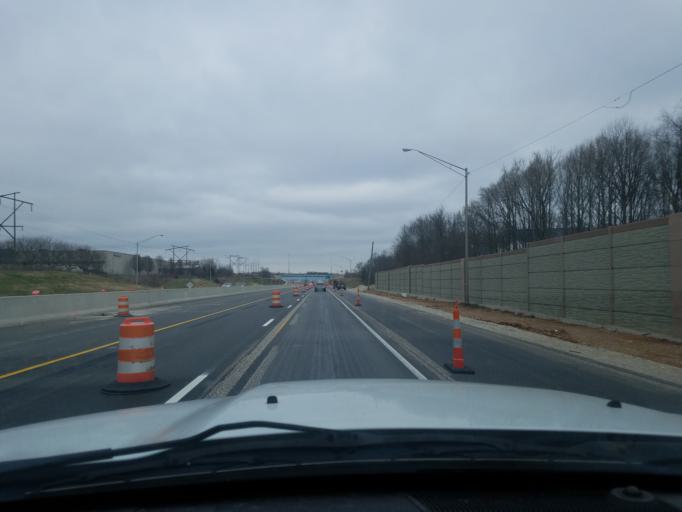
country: US
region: Indiana
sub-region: Monroe County
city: Bloomington
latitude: 39.1563
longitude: -86.5729
